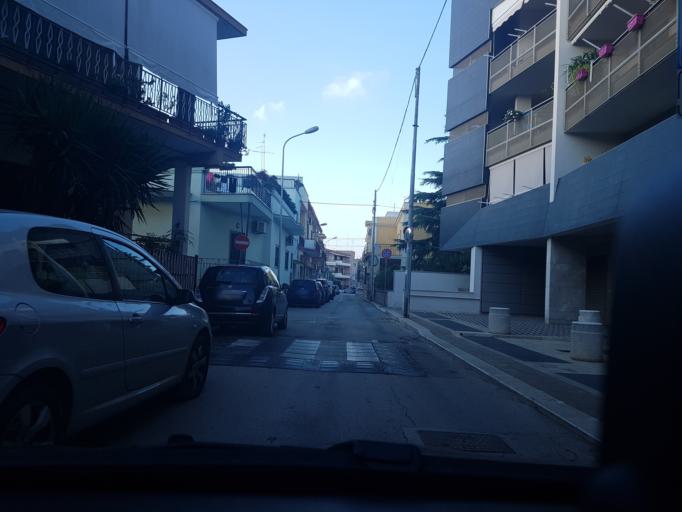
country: IT
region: Apulia
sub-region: Provincia di Bari
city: Bitritto
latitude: 41.0389
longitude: 16.8287
